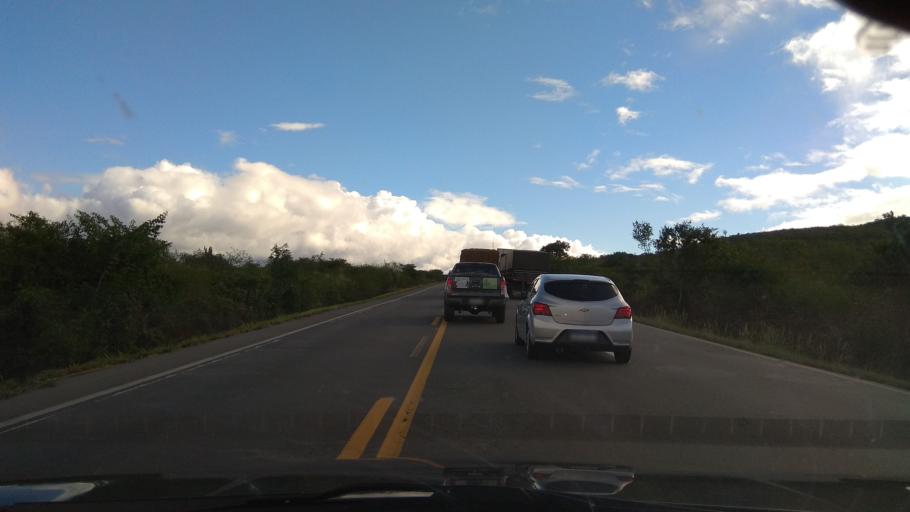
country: BR
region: Bahia
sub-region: Castro Alves
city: Castro Alves
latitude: -12.6523
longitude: -39.6119
